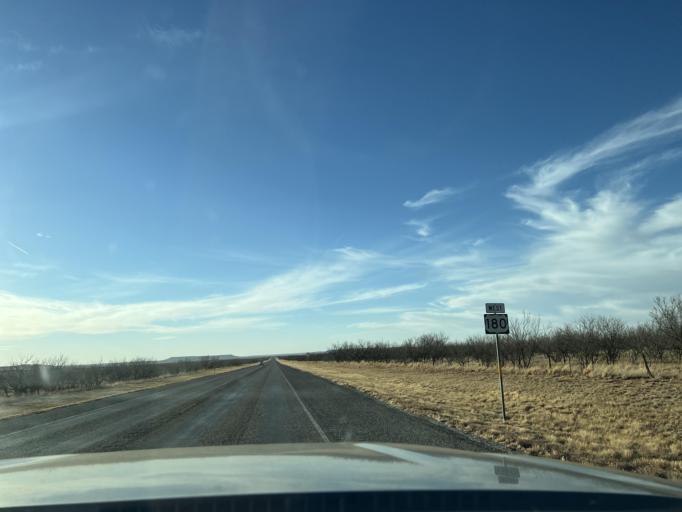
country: US
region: Texas
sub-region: Borden County
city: Gail
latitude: 32.7662
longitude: -101.2909
